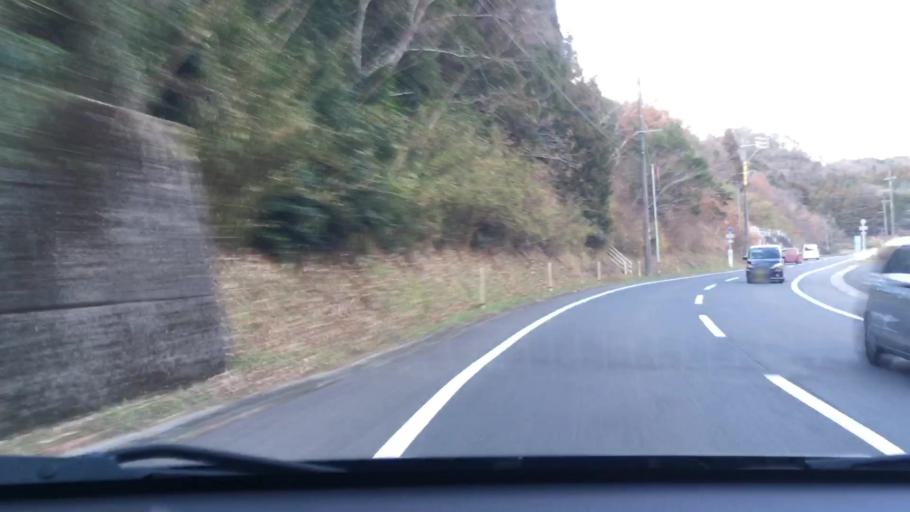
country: JP
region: Oita
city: Bungo-Takada-shi
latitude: 33.4706
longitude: 131.3848
